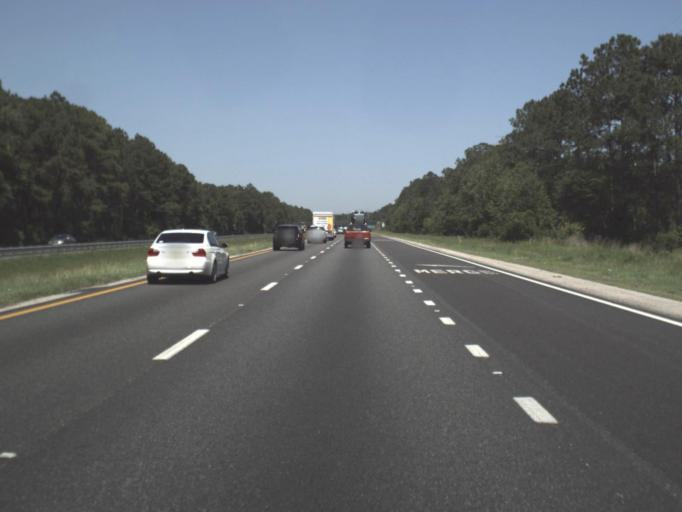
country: US
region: Florida
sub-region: Duval County
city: Baldwin
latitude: 30.2895
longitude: -81.9734
